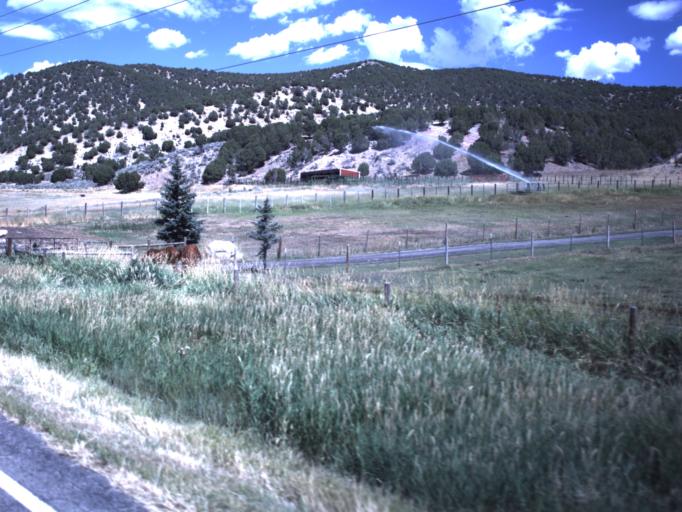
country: US
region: Utah
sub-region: Summit County
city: Oakley
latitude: 40.7446
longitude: -111.3594
